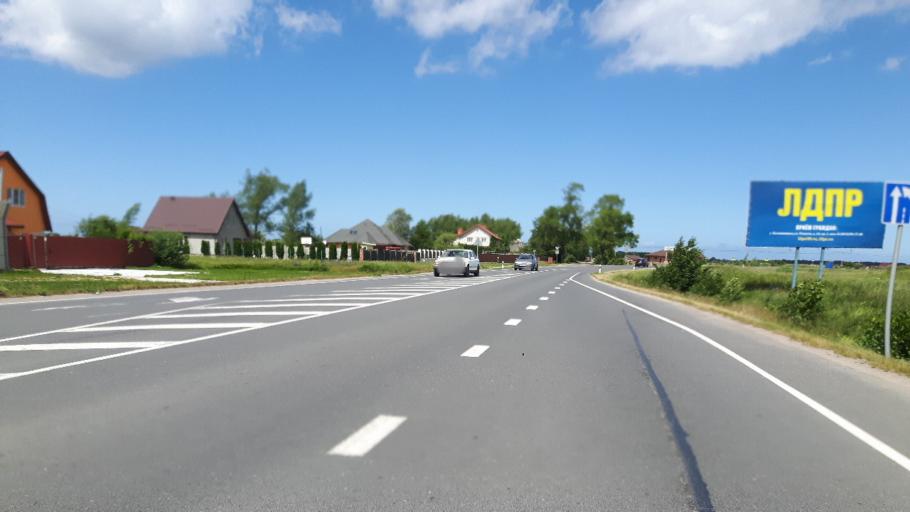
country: RU
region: Kaliningrad
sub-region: Zelenogradskiy Rayon
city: Zelenogradsk
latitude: 54.9246
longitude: 20.3981
